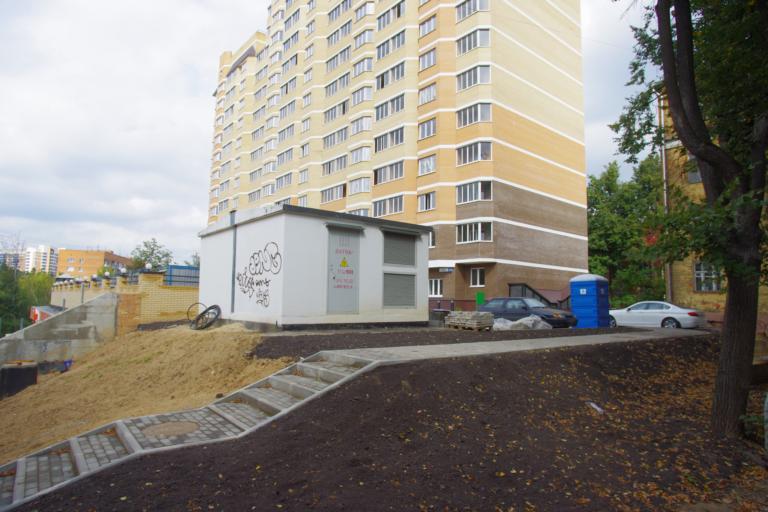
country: RU
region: Moskovskaya
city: Krasnogorsk
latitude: 55.8314
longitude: 37.3272
